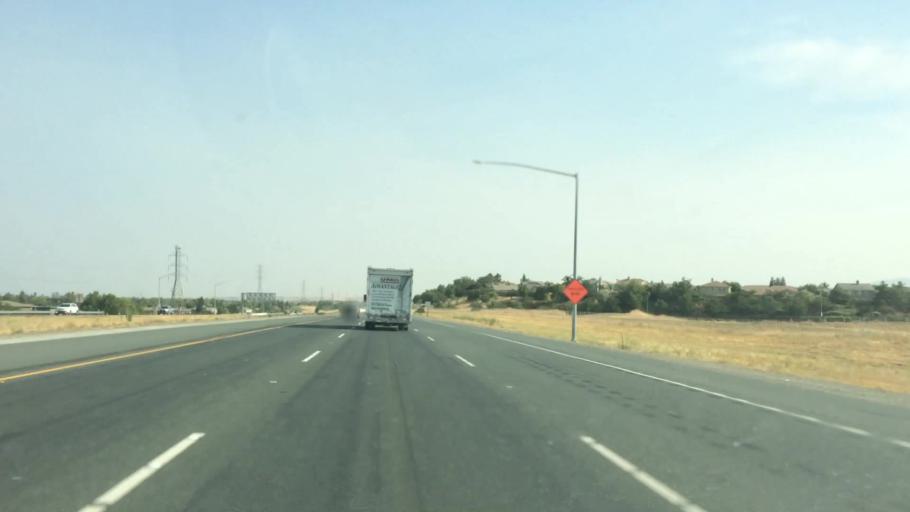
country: US
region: California
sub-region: Contra Costa County
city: Brentwood
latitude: 37.9447
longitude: -121.7424
